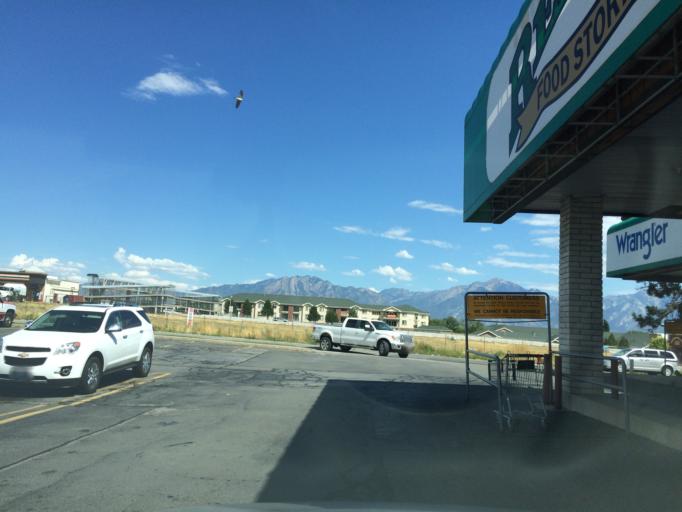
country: US
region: Utah
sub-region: Salt Lake County
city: Kearns
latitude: 40.6376
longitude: -111.9787
